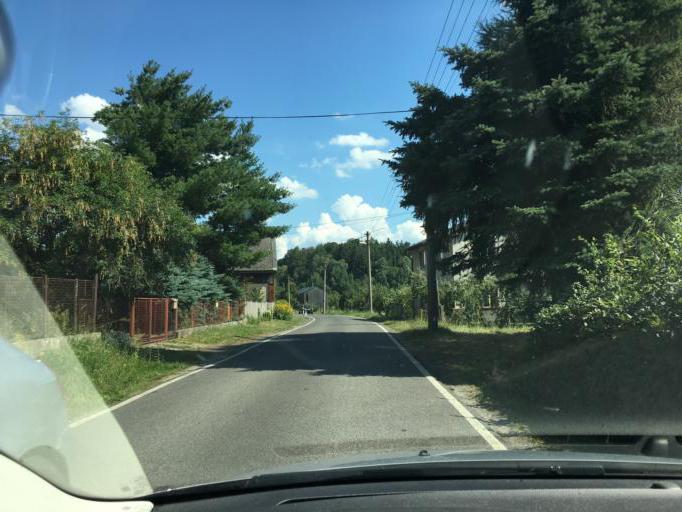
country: CZ
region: Liberecky
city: Mala Skala
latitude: 50.6498
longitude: 15.1600
